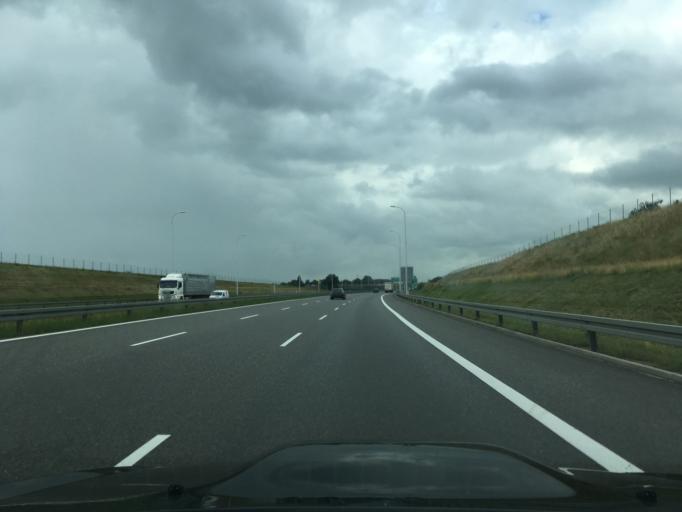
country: PL
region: Lublin Voivodeship
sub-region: Powiat lubelski
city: Lublin
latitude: 51.2982
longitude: 22.5266
